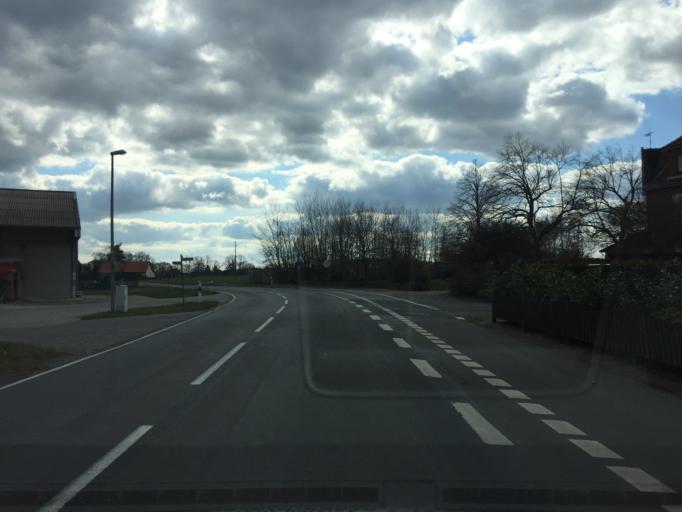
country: DE
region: Lower Saxony
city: Maasen
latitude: 52.6979
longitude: 8.8918
